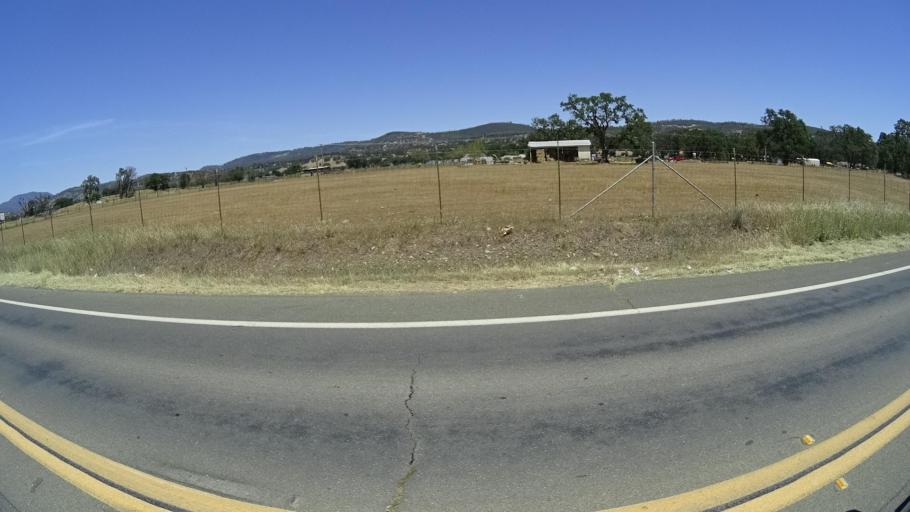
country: US
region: California
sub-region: Lake County
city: Hidden Valley Lake
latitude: 38.7909
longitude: -122.5600
